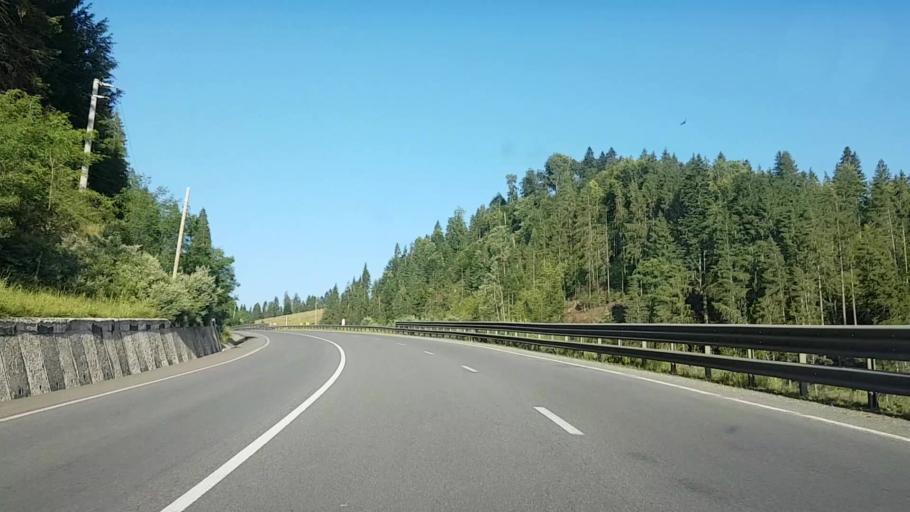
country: RO
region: Bistrita-Nasaud
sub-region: Comuna Lunca Ilvei
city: Lunca Ilvei
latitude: 47.2272
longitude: 24.9709
